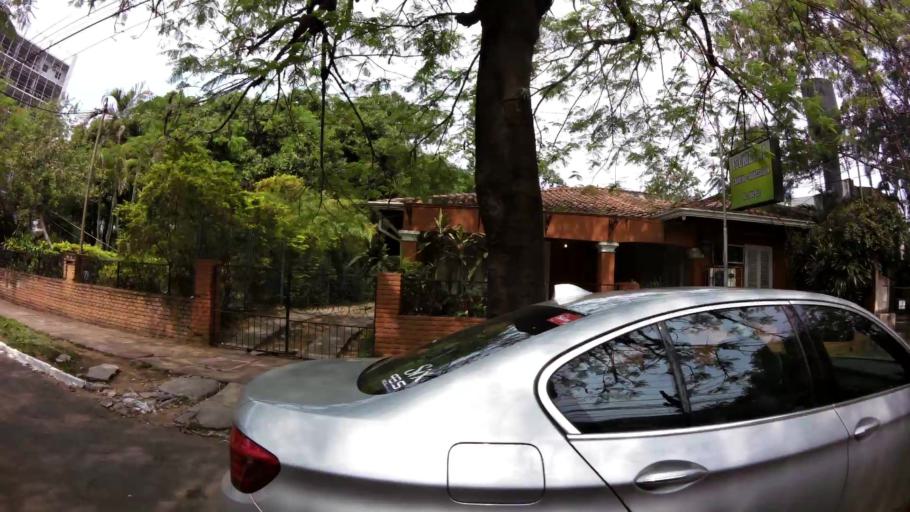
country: PY
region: Asuncion
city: Asuncion
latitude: -25.2938
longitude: -57.5772
